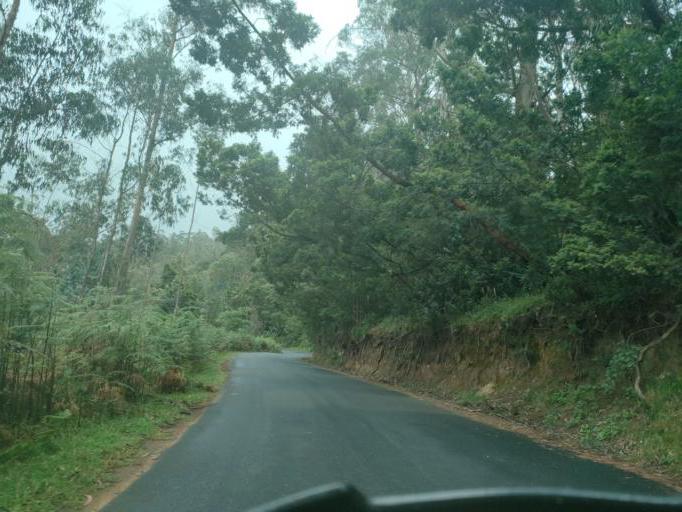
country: IN
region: Tamil Nadu
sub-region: Dindigul
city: Kodaikanal
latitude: 10.2425
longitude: 77.3645
